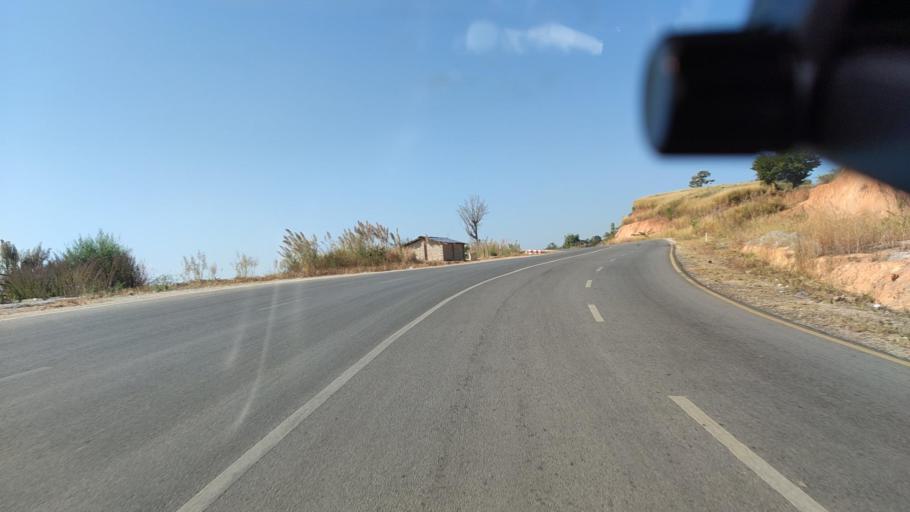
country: MM
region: Shan
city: Lashio
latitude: 23.3249
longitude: 97.9757
